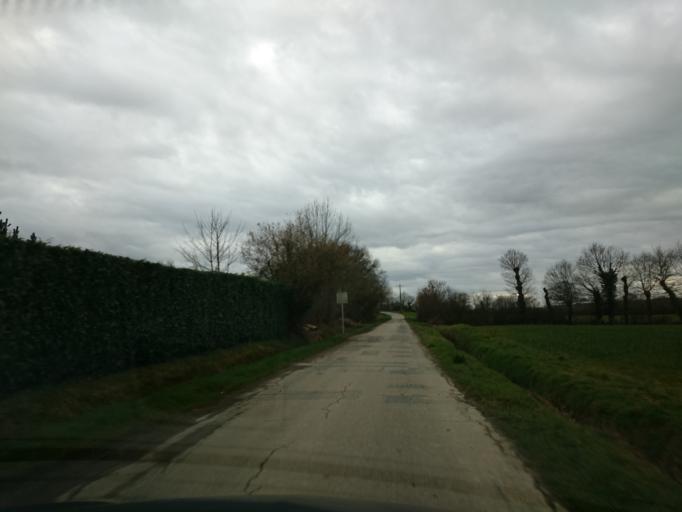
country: FR
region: Brittany
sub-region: Departement d'Ille-et-Vilaine
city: Crevin
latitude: 47.9218
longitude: -1.6333
